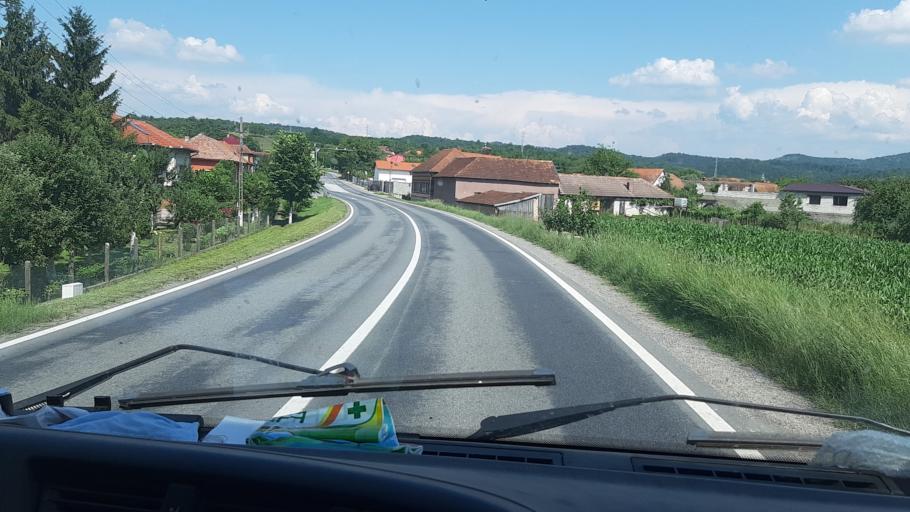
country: RO
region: Caras-Severin
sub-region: Comuna Ezeris
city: Ezeris
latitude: 45.3767
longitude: 21.9369
